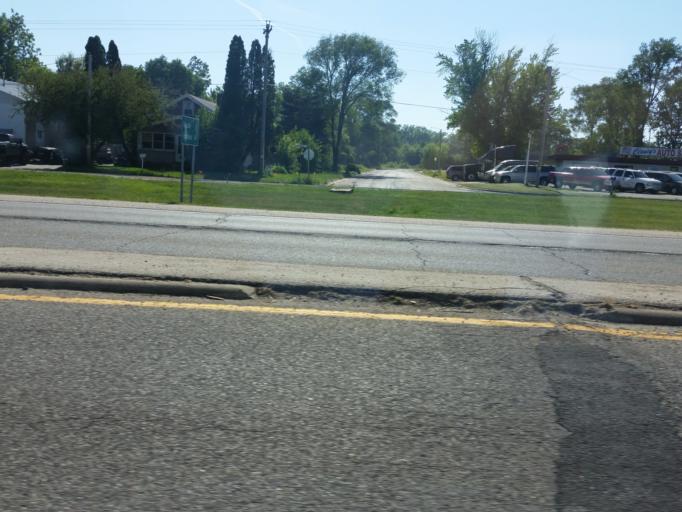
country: US
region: Illinois
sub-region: Winnebago County
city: South Beloit
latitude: 42.4911
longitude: -89.0196
